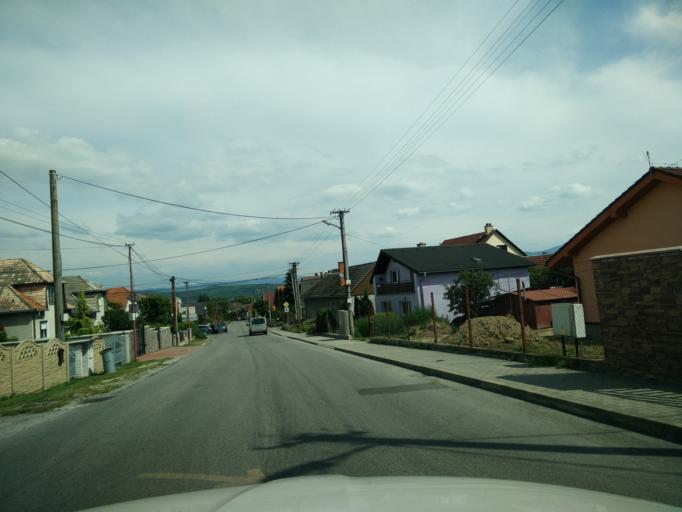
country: SK
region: Nitriansky
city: Bojnice
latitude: 48.8212
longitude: 18.6141
